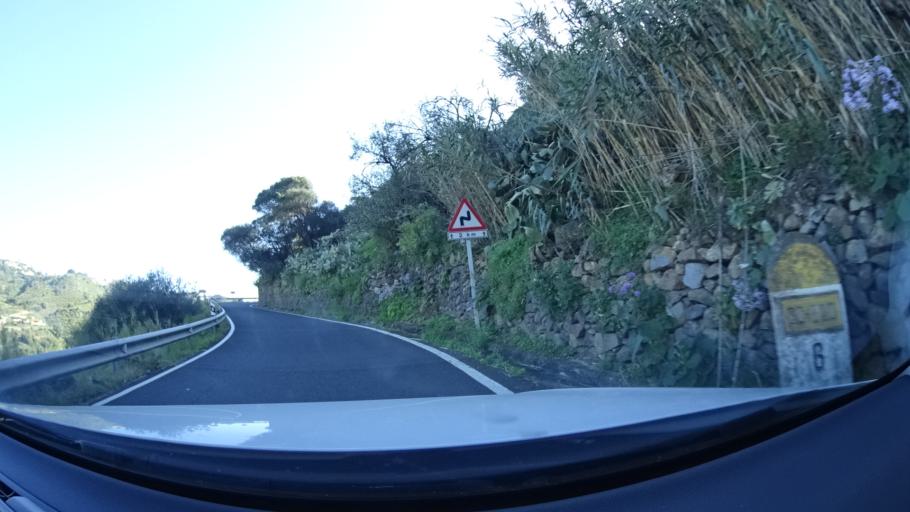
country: ES
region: Canary Islands
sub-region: Provincia de Las Palmas
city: Santa Brigida
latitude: 28.0193
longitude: -15.4729
